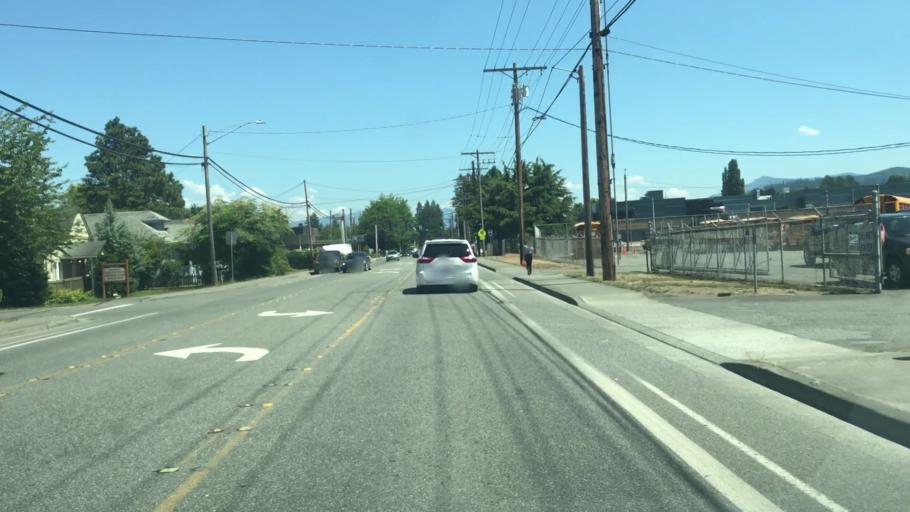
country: US
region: Washington
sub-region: Snohomish County
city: Monroe
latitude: 47.8505
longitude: -121.9926
